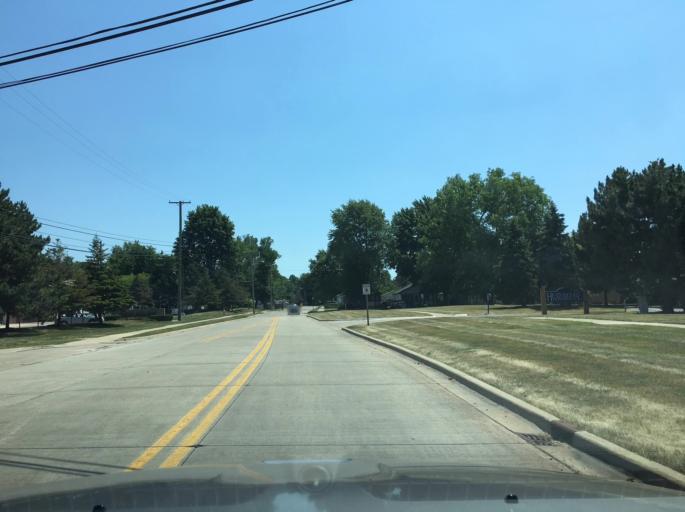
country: US
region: Michigan
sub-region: Macomb County
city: Clinton
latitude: 42.5540
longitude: -82.9103
